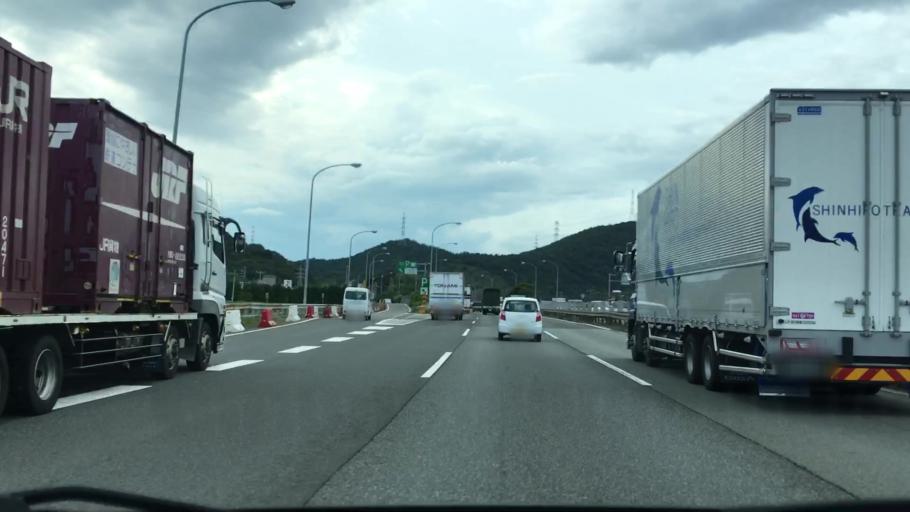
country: JP
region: Hyogo
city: Shirahamacho-usazakiminami
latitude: 34.7994
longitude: 134.7554
